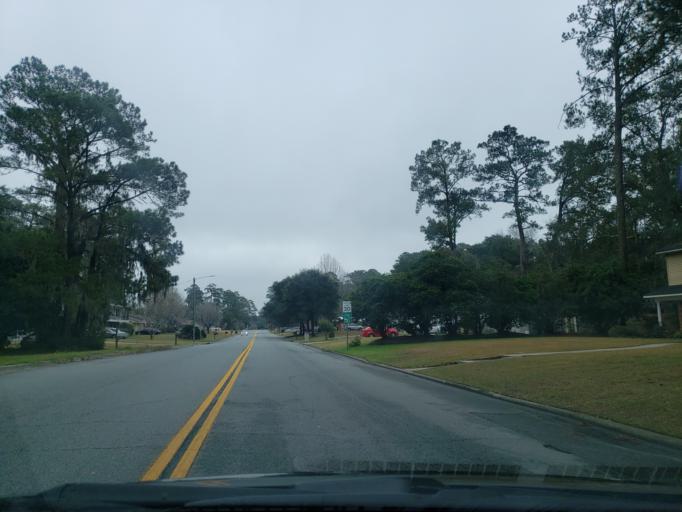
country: US
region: Georgia
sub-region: Chatham County
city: Montgomery
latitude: 31.9734
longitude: -81.1581
